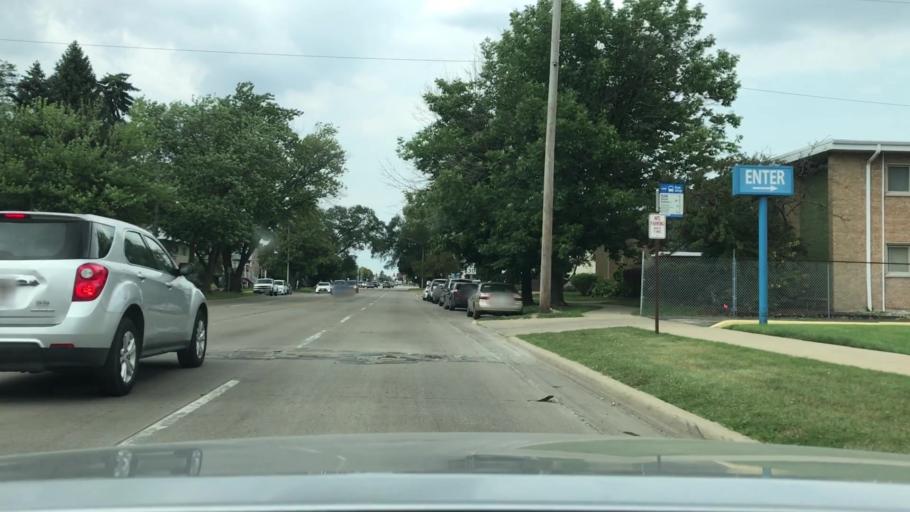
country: US
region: Illinois
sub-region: Cook County
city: Evergreen Park
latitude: 41.7167
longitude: -87.7017
